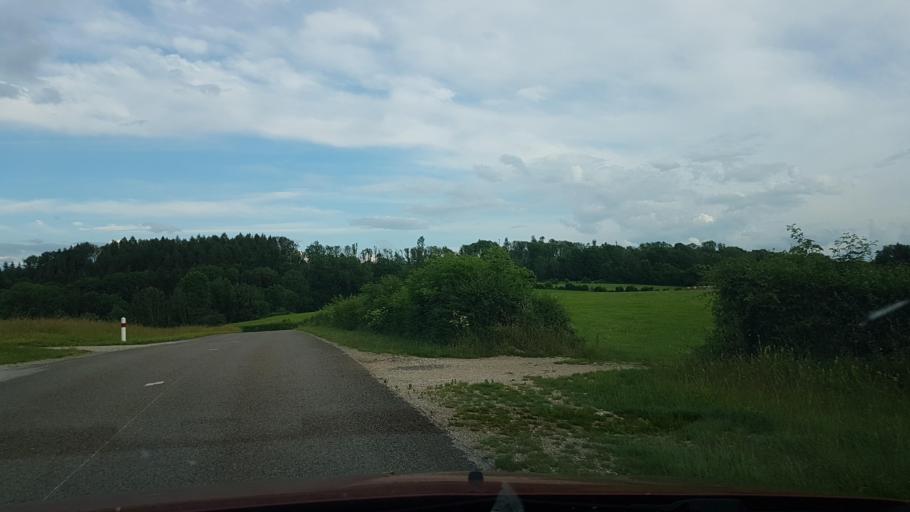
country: FR
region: Franche-Comte
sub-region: Departement du Jura
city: Clairvaux-les-Lacs
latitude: 46.5754
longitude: 5.7398
